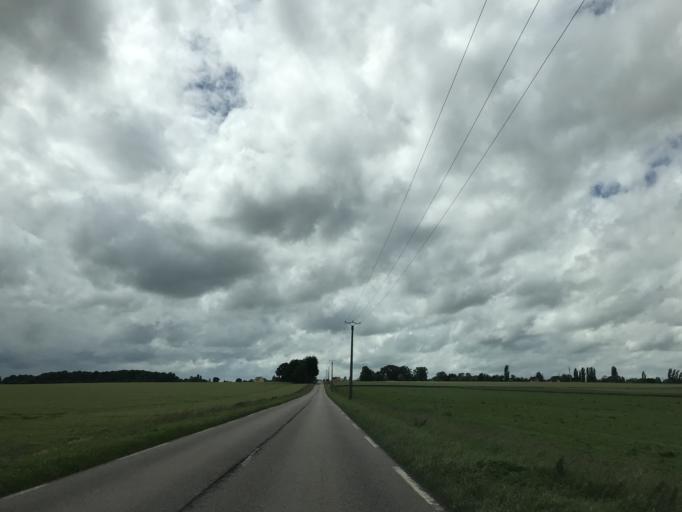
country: FR
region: Ile-de-France
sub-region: Departement des Yvelines
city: Breval
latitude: 48.9588
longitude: 1.5207
